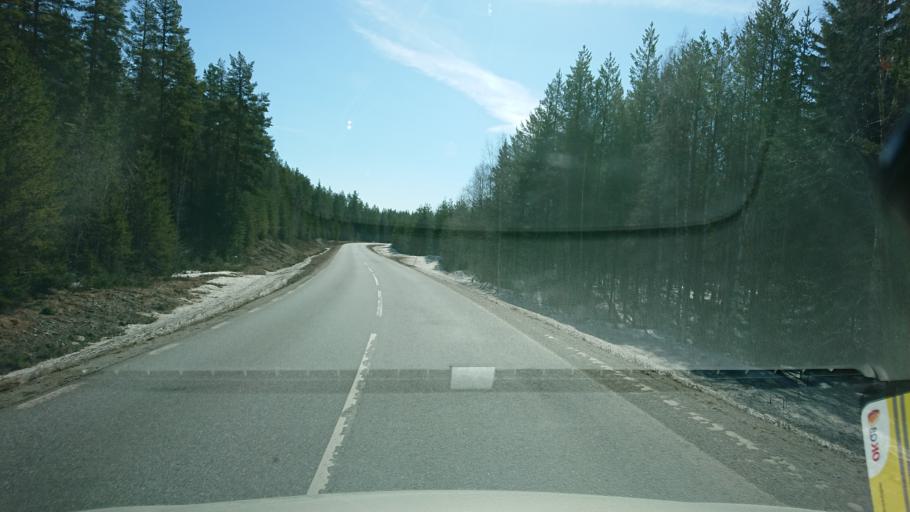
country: SE
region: Vaesterbotten
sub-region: Dorotea Kommun
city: Dorotea
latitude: 64.0145
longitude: 16.2894
